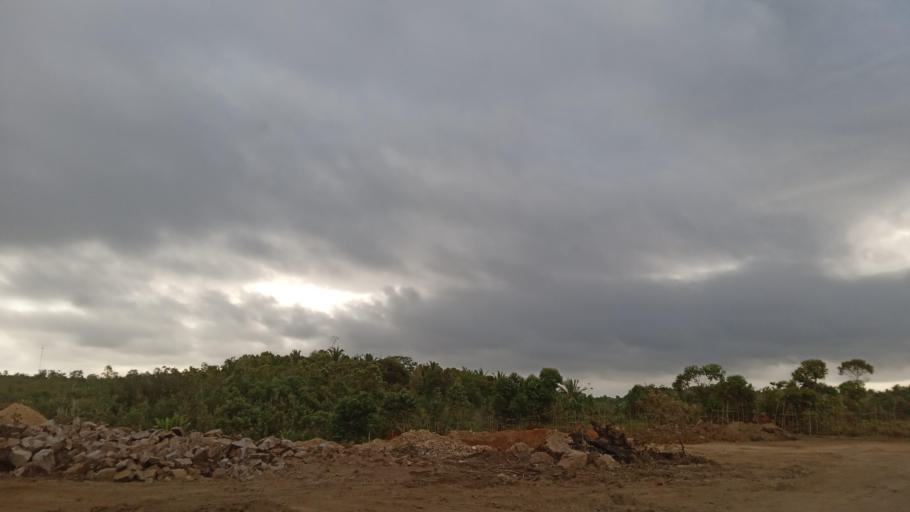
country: MG
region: Atsimo-Atsinanana
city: Vohipaho
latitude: -23.6161
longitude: 47.6035
